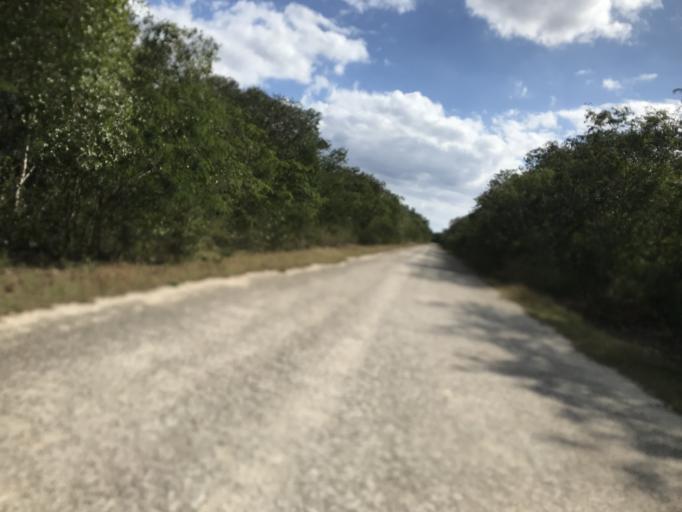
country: CU
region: Cienfuegos
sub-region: Municipio de Aguada de Pasajeros
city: Aguada de Pasajeros
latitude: 22.0751
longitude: -81.0366
